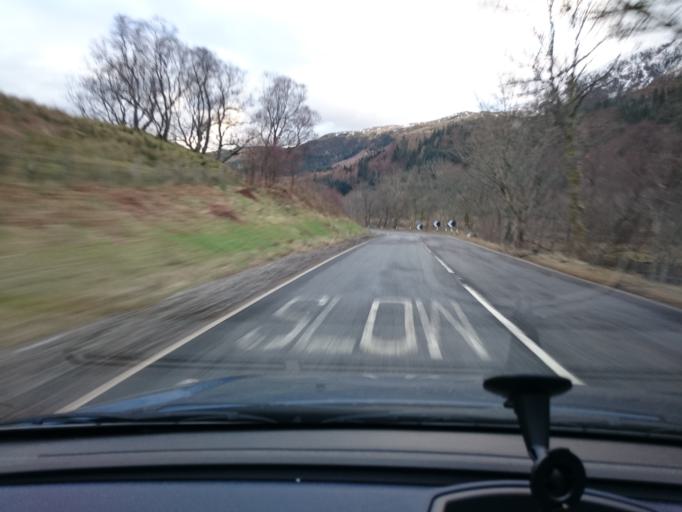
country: GB
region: Scotland
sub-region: Stirling
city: Callander
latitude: 56.2652
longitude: -4.2861
